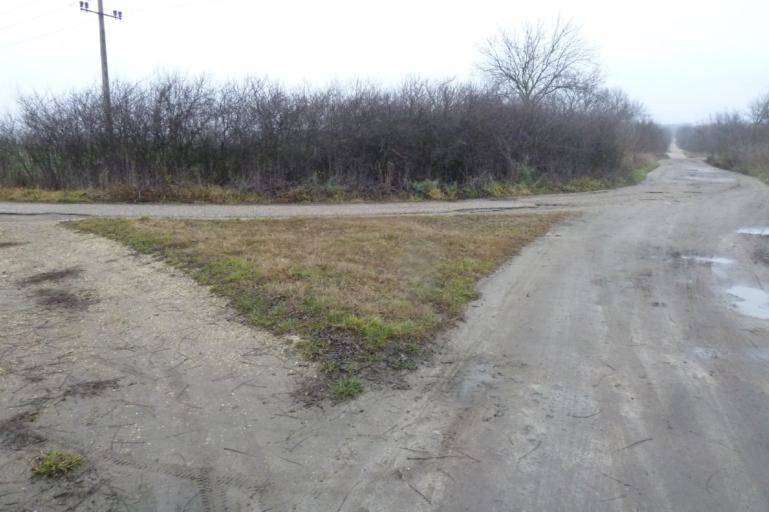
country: HU
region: Pest
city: Pilis
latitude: 47.2964
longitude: 19.5725
